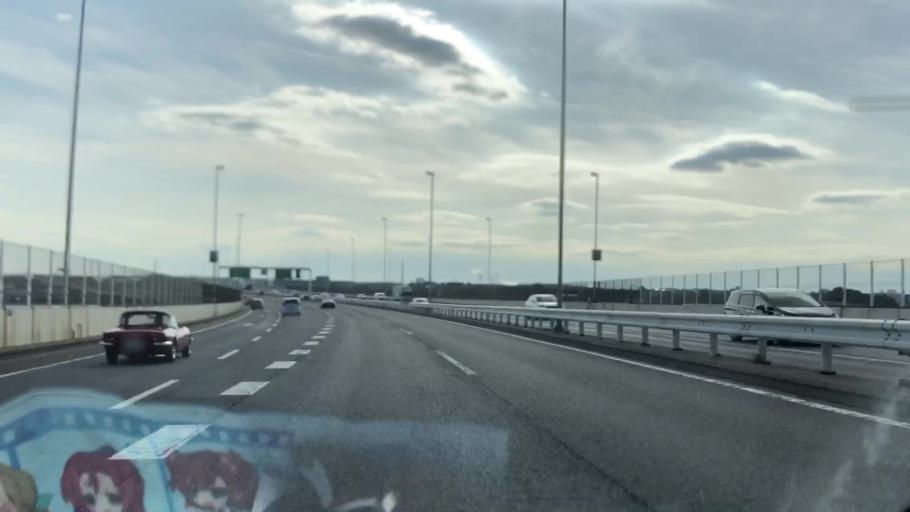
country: JP
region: Kanagawa
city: Yokohama
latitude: 35.4456
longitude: 139.6682
